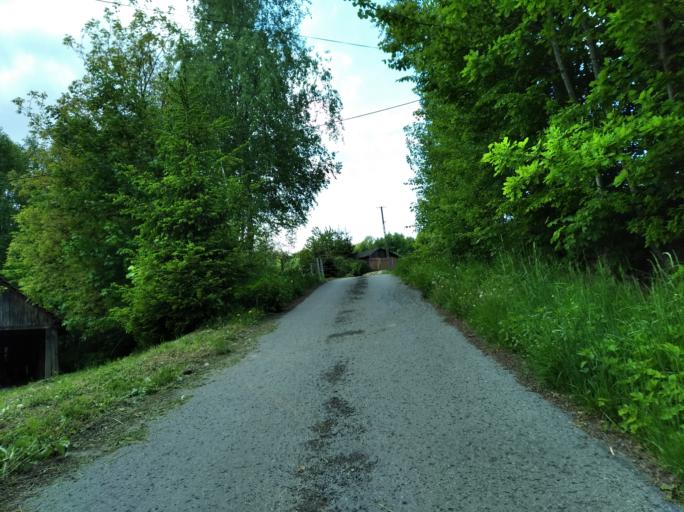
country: PL
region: Subcarpathian Voivodeship
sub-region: Powiat ropczycko-sedziszowski
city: Wielopole Skrzynskie
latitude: 49.9240
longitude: 21.6217
